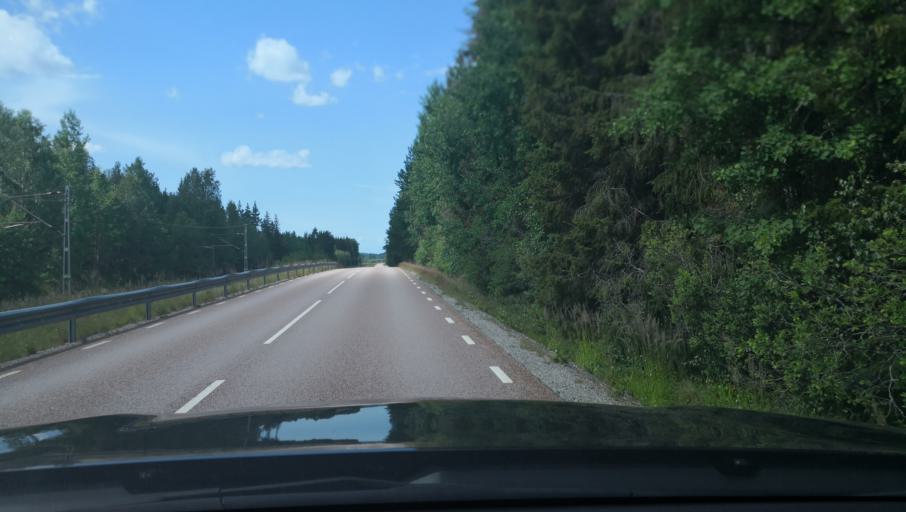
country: SE
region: Vaestmanland
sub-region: Surahammars Kommun
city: Ramnas
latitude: 59.8443
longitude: 16.1125
